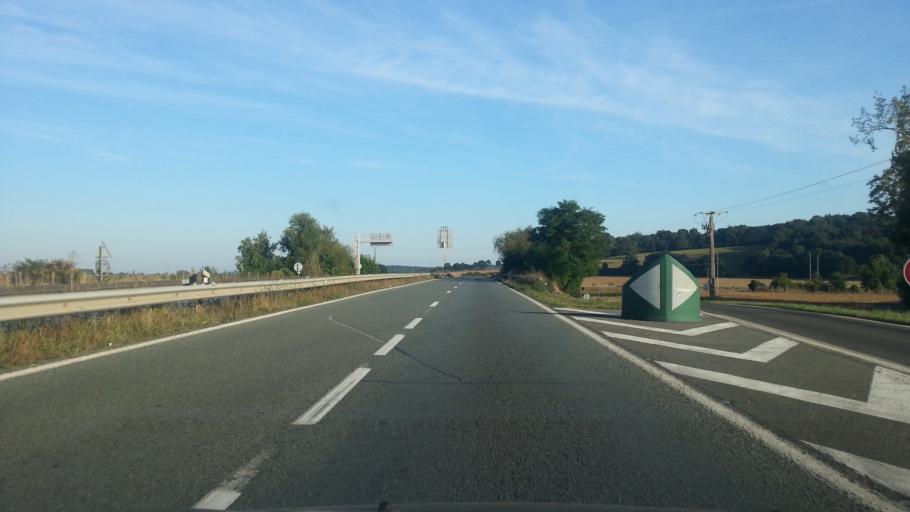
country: FR
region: Picardie
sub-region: Departement de l'Oise
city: Warluis
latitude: 49.4204
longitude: 2.1603
